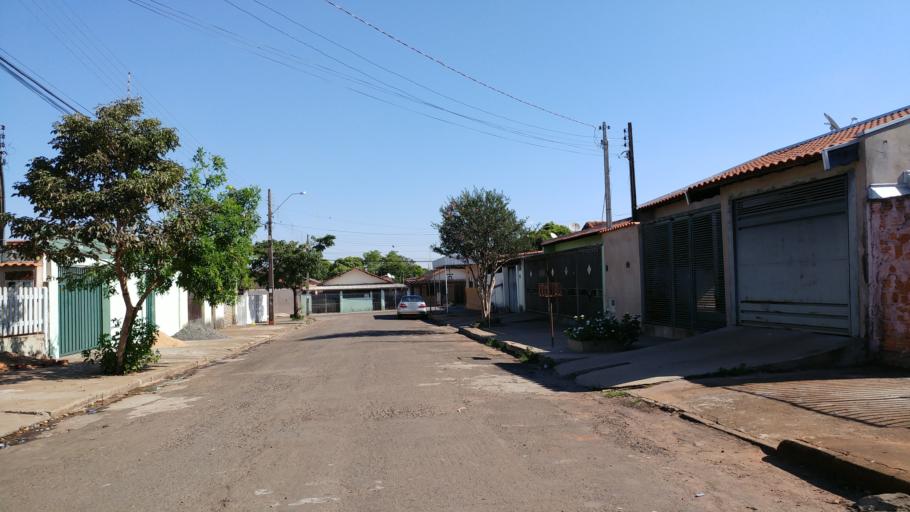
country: BR
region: Sao Paulo
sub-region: Paraguacu Paulista
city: Paraguacu Paulista
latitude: -22.4324
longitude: -50.5826
